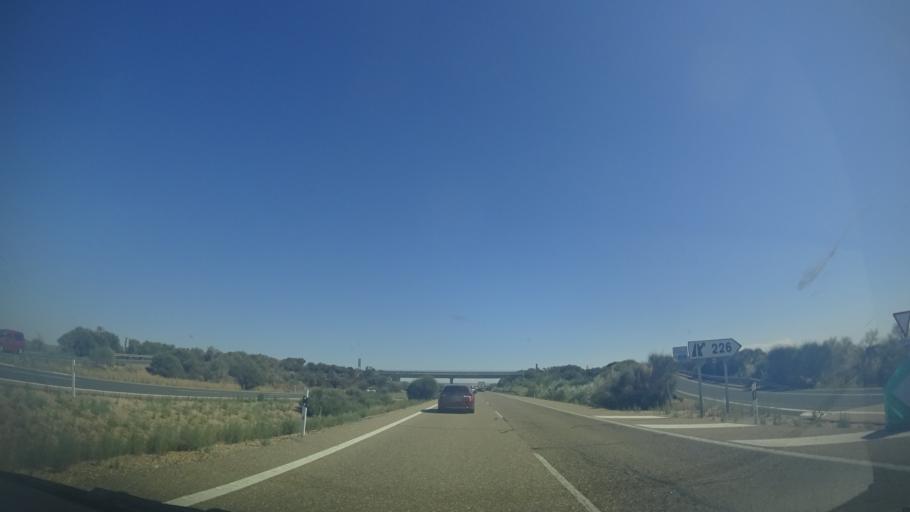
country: ES
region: Castille and Leon
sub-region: Provincia de Zamora
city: Quintanilla del Monte
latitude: 41.8015
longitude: -5.3458
